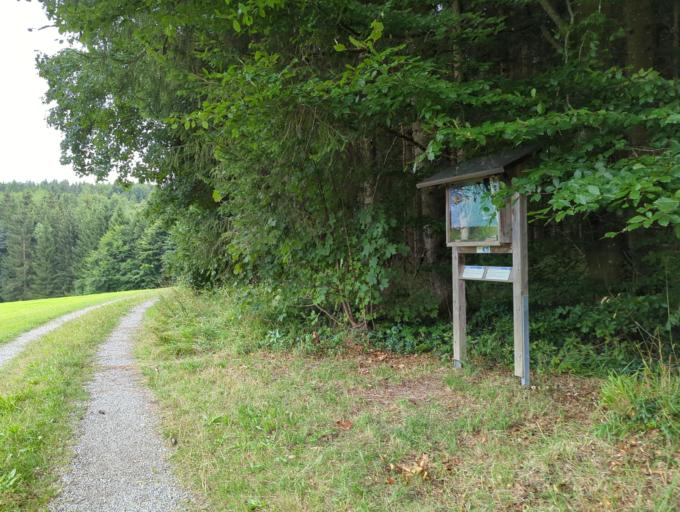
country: DE
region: Bavaria
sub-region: Swabia
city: Friesenried
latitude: 47.8656
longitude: 10.5497
